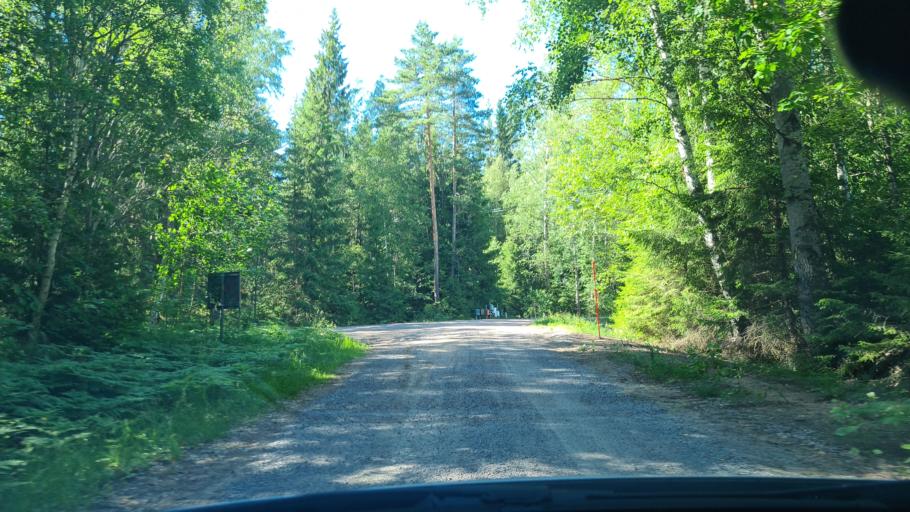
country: SE
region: OEstergoetland
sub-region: Norrkopings Kommun
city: Krokek
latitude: 58.7025
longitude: 16.4326
